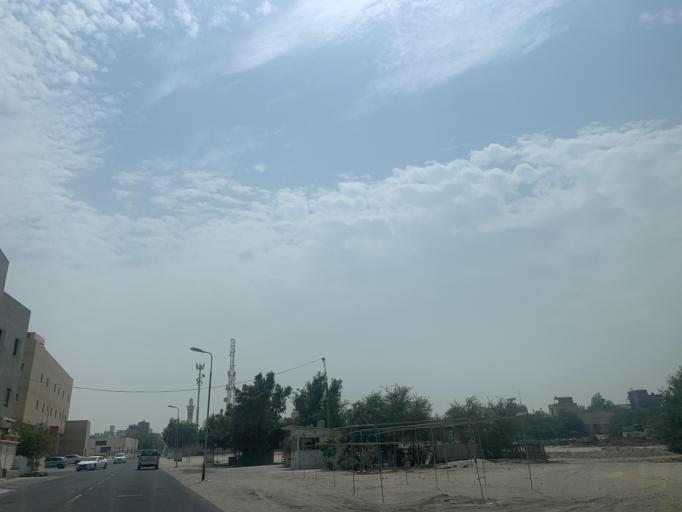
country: BH
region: Manama
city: Jidd Hafs
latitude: 26.2123
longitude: 50.5074
